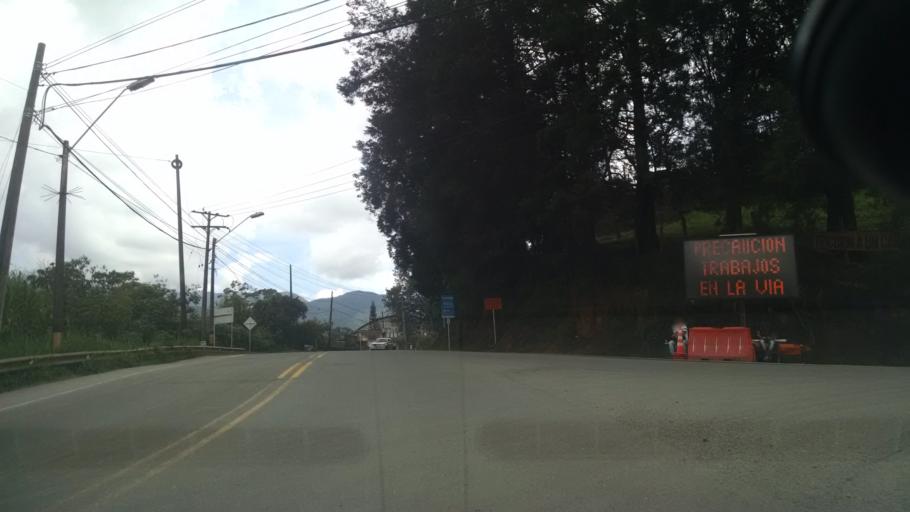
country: CO
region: Antioquia
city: Caldas
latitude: 6.0690
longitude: -75.6336
